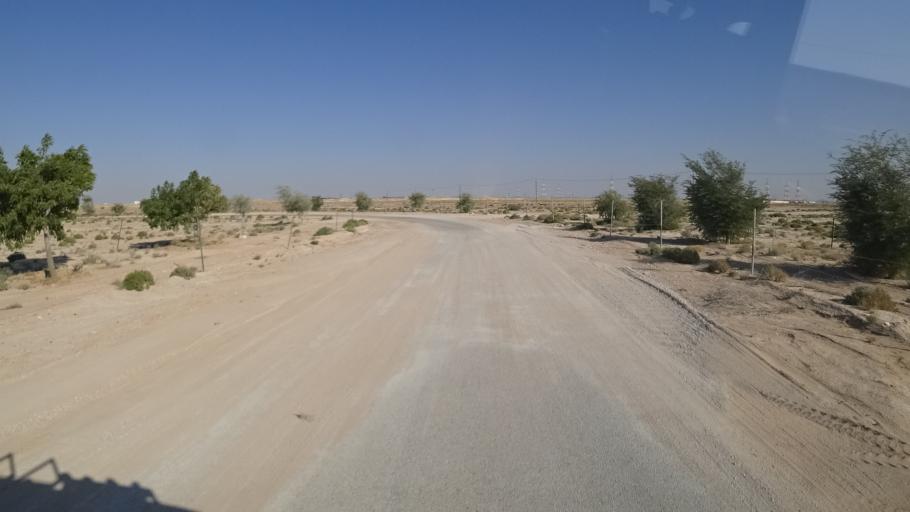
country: OM
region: Zufar
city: Salalah
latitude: 17.5943
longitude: 54.0317
